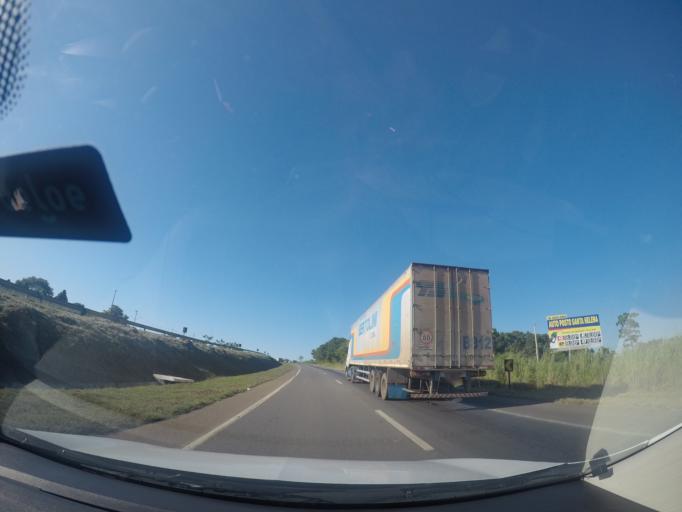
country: BR
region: Goias
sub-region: Aparecida De Goiania
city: Aparecida de Goiania
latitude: -16.8930
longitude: -49.2556
